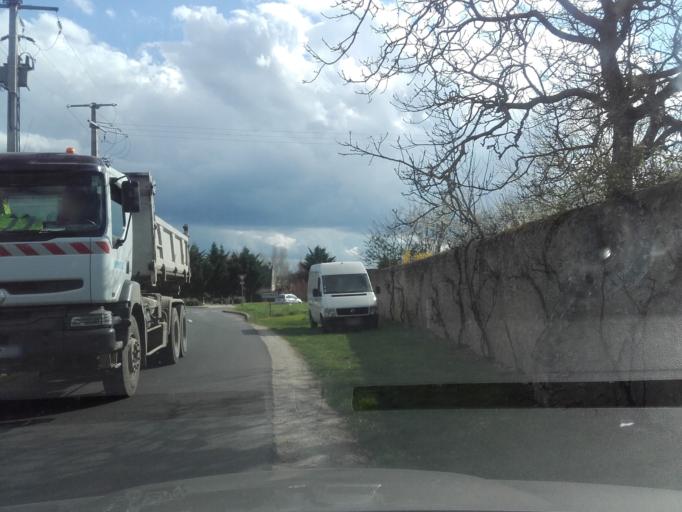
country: FR
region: Centre
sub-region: Departement d'Indre-et-Loire
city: Luynes
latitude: 47.4026
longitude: 0.5550
